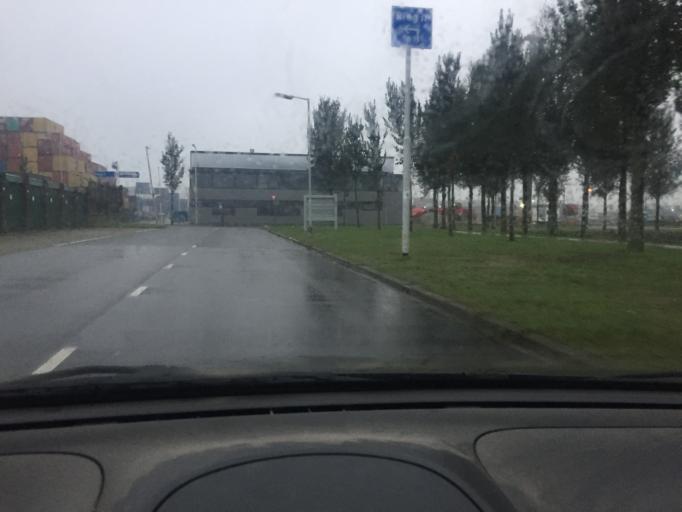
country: NL
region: South Holland
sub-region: Gemeente Albrandswaard
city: Rhoon
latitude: 51.8923
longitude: 4.4134
